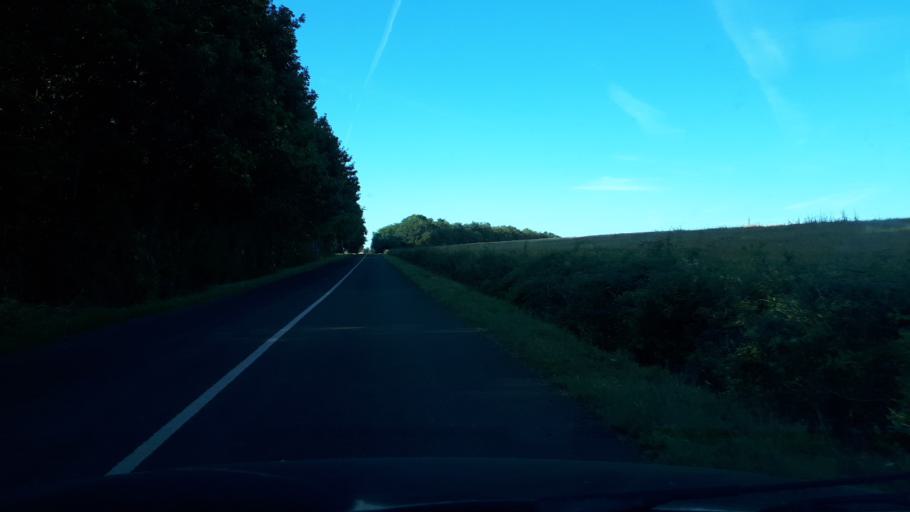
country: FR
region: Centre
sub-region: Departement du Loir-et-Cher
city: Lunay
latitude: 47.7476
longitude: 0.9391
